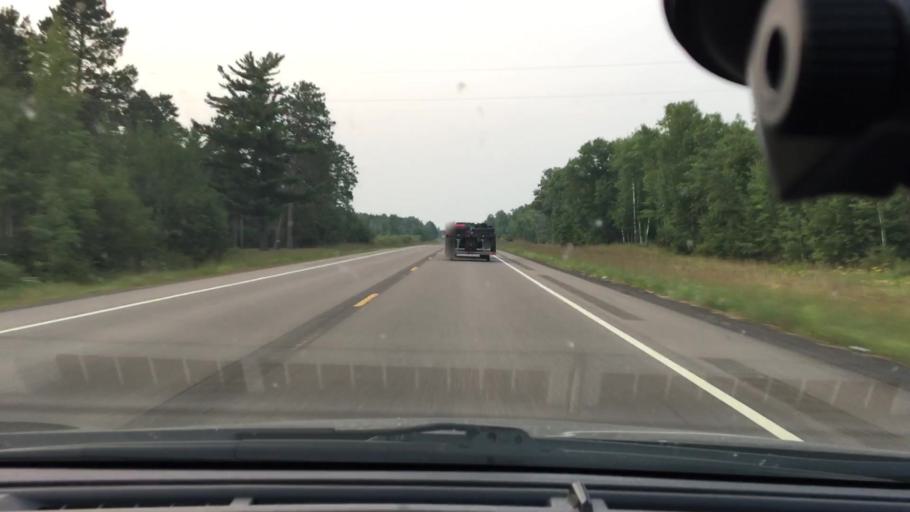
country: US
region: Minnesota
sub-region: Crow Wing County
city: Crosby
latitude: 46.5885
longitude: -93.9515
